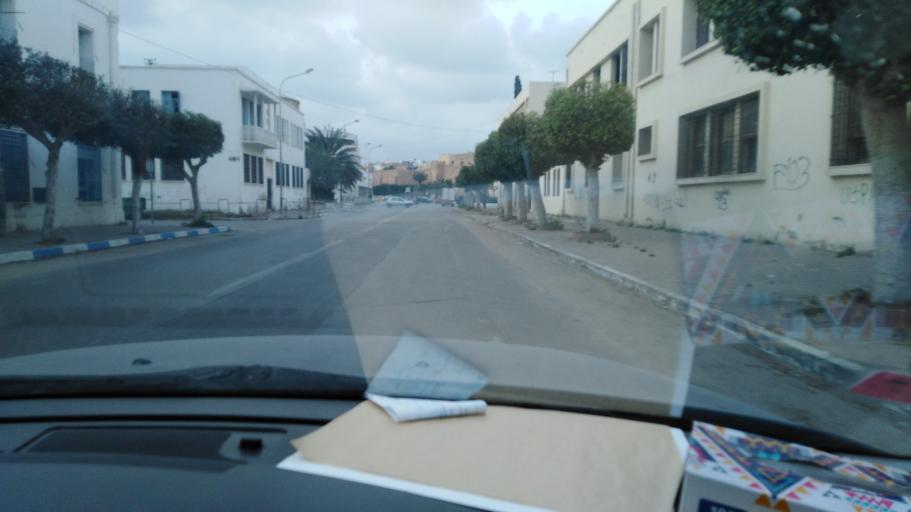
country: TN
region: Safaqis
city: Sfax
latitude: 34.7317
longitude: 10.7585
